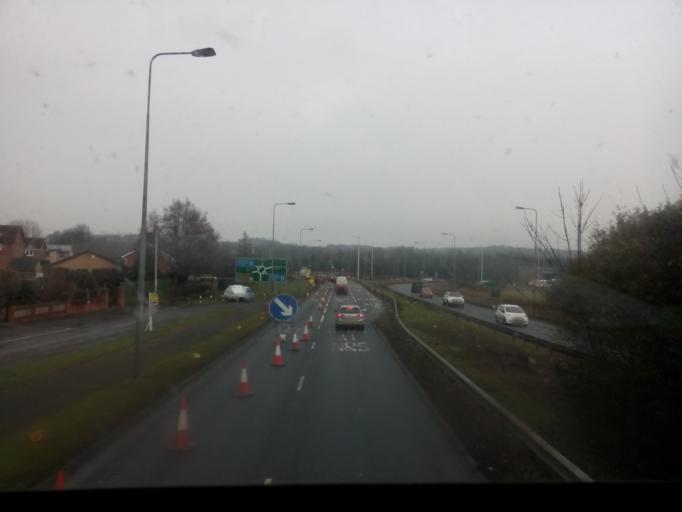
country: GB
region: England
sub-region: County Durham
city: Chester-le-Street
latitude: 54.8639
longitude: -1.5669
